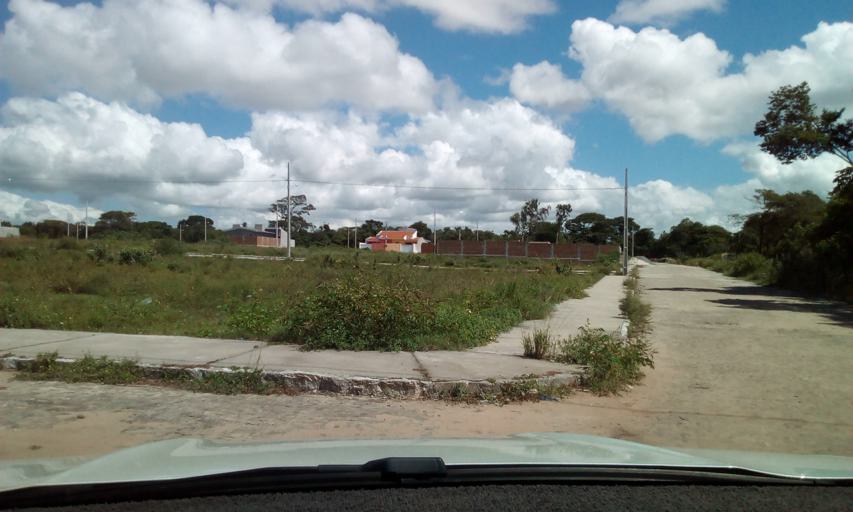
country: BR
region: Paraiba
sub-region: Joao Pessoa
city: Joao Pessoa
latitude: -7.1738
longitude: -34.8219
